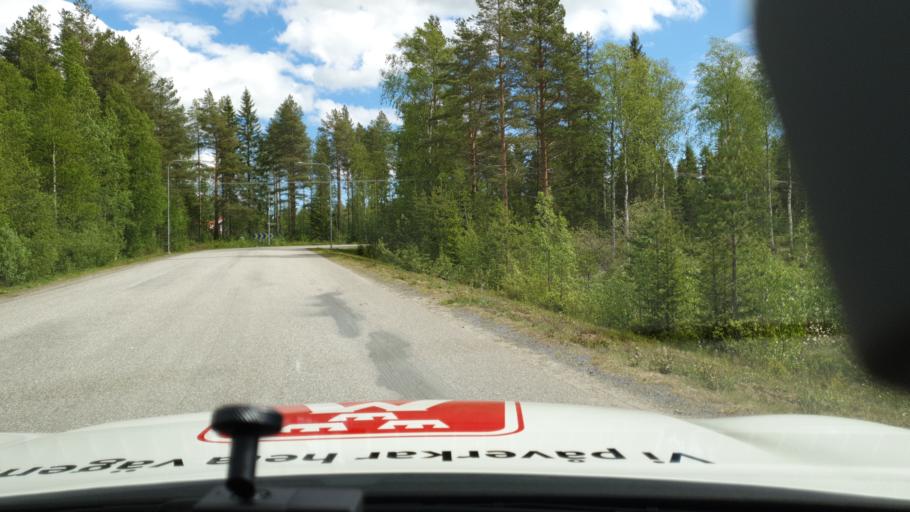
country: SE
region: Vaesterbotten
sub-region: Umea Kommun
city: Ersmark
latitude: 63.8636
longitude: 20.3437
